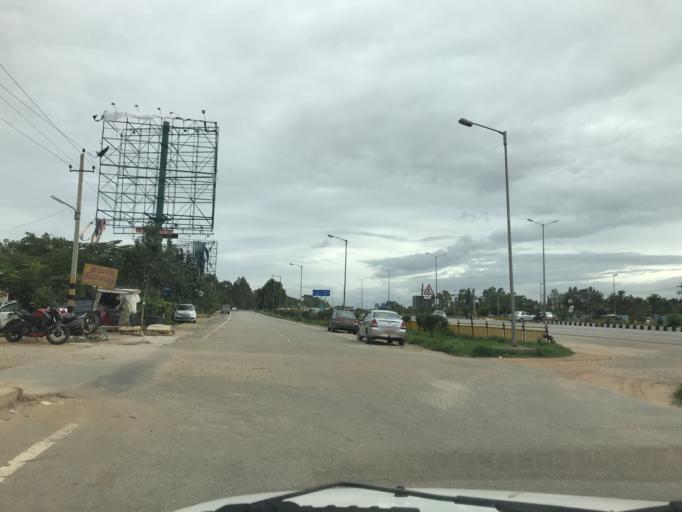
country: IN
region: Karnataka
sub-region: Bangalore Rural
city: Devanhalli
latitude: 13.2060
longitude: 77.6678
